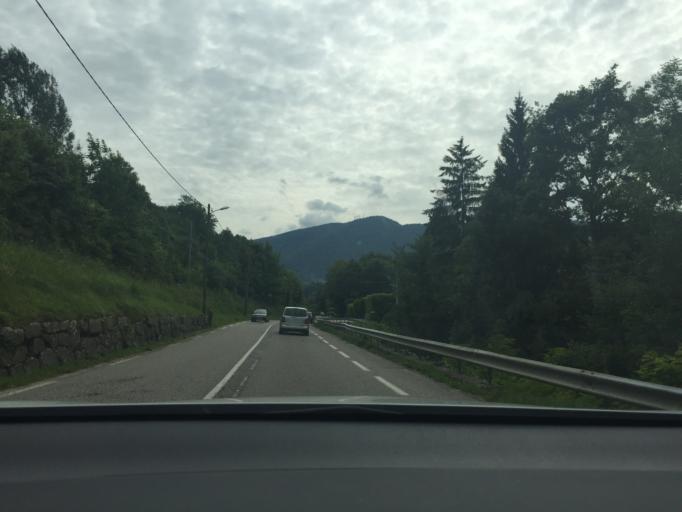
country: FR
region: Rhone-Alpes
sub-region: Departement de la Savoie
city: Vimines
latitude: 45.5453
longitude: 5.8837
